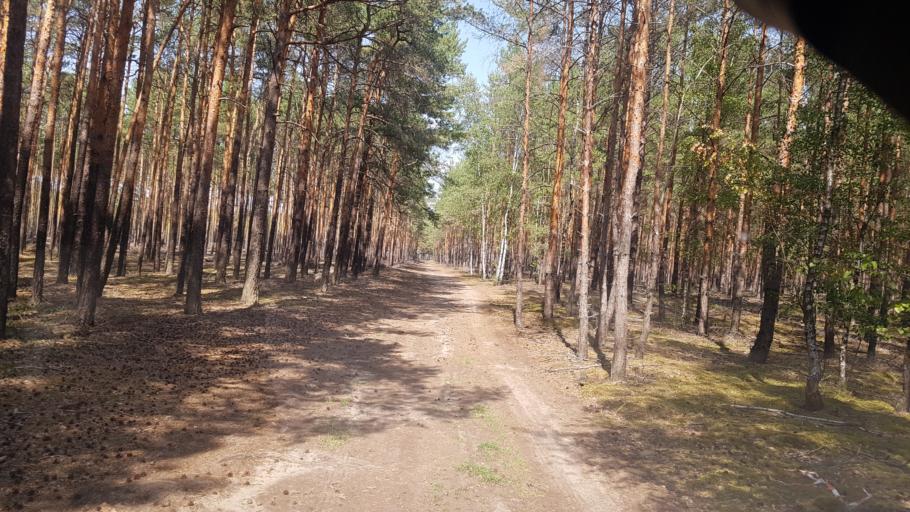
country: DE
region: Brandenburg
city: Spremberg
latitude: 51.6394
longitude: 14.4099
